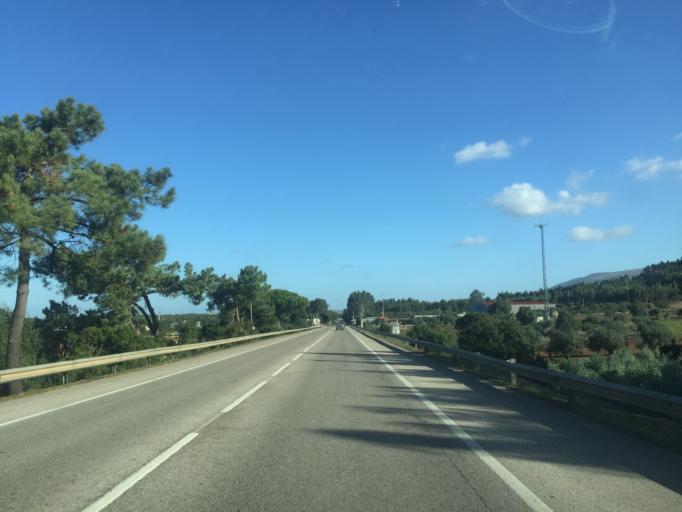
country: PT
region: Leiria
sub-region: Alcobaca
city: Turquel
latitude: 39.4895
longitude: -8.9330
